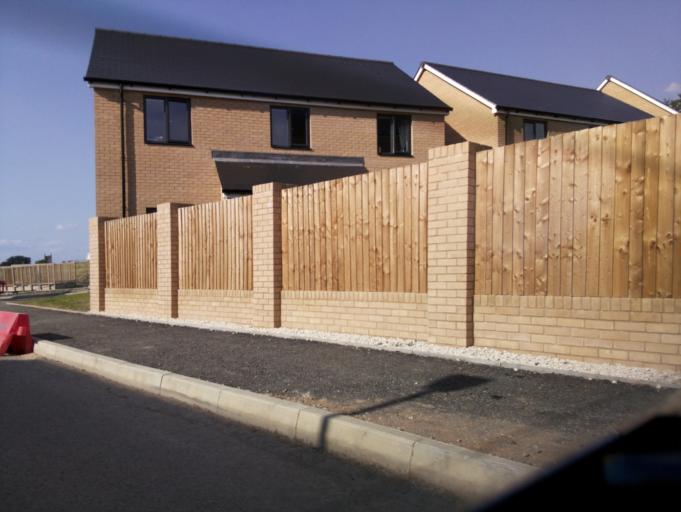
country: GB
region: England
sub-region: Gloucestershire
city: Dursley
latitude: 51.6861
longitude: -2.3519
